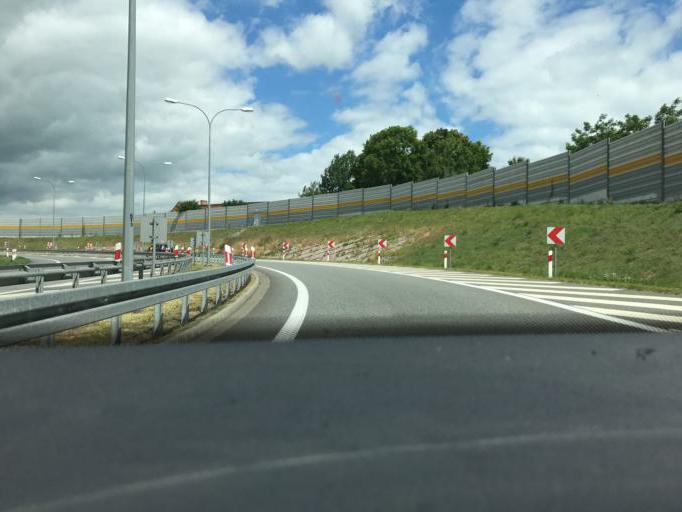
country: PL
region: Kujawsko-Pomorskie
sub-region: Powiat torunski
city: Lubicz Dolny
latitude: 53.0362
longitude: 18.7448
